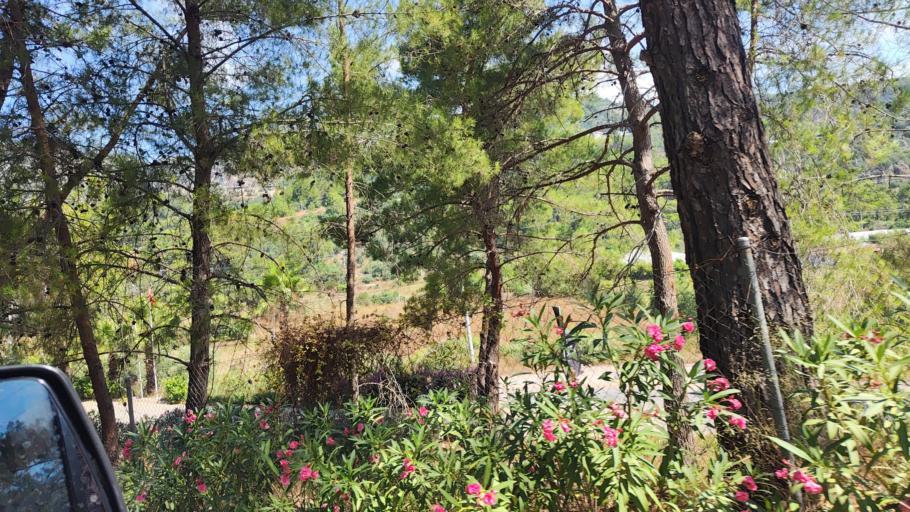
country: TR
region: Mugla
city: Sarigerme
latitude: 36.7072
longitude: 28.6951
